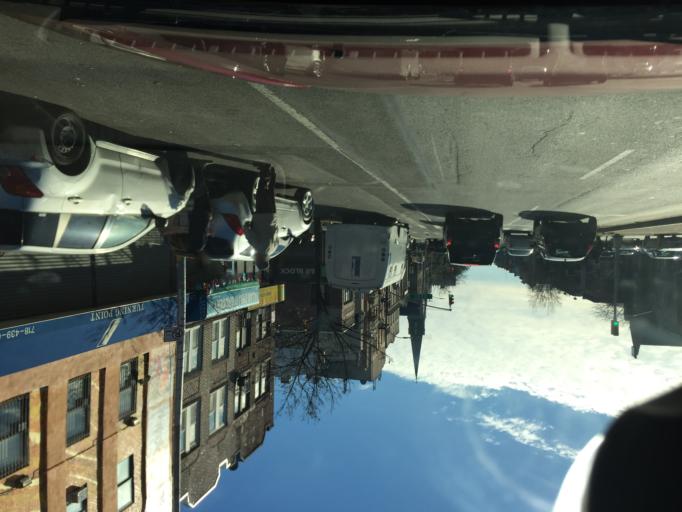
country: US
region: New York
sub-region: Kings County
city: Bensonhurst
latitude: 40.6452
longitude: -74.0141
